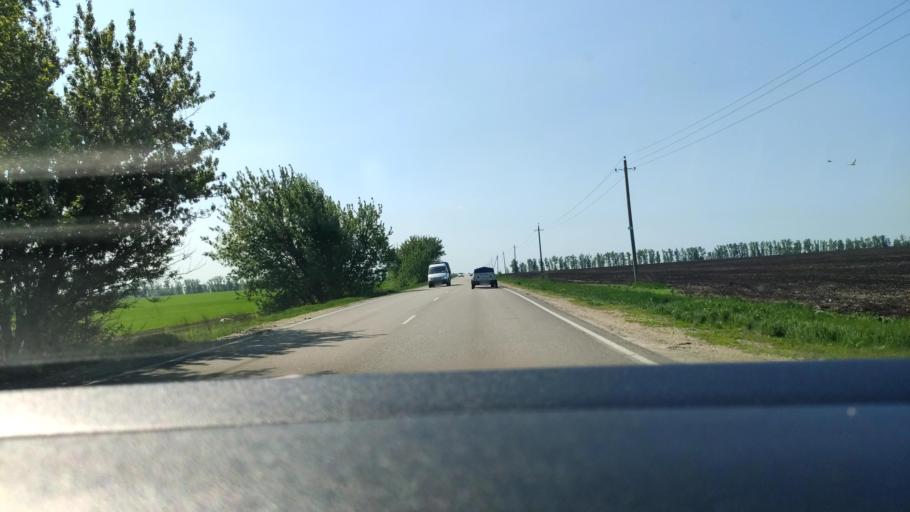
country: RU
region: Voronezj
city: Novaya Usman'
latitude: 51.5718
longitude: 39.3749
